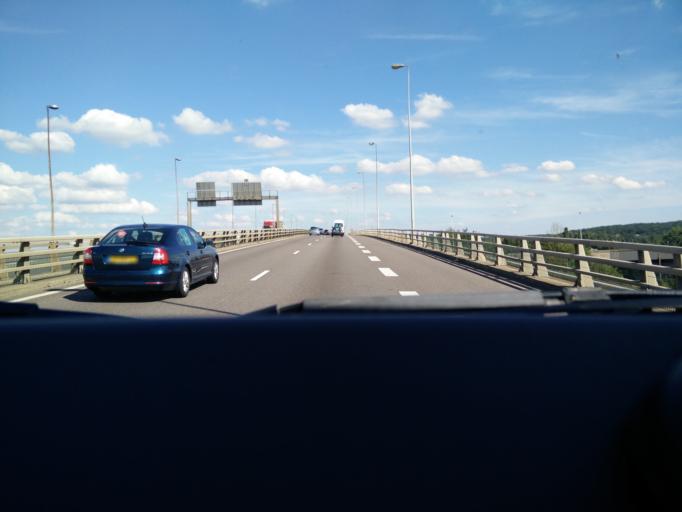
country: FR
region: Lorraine
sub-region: Departement de la Moselle
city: Thionville
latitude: 49.3485
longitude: 6.1585
